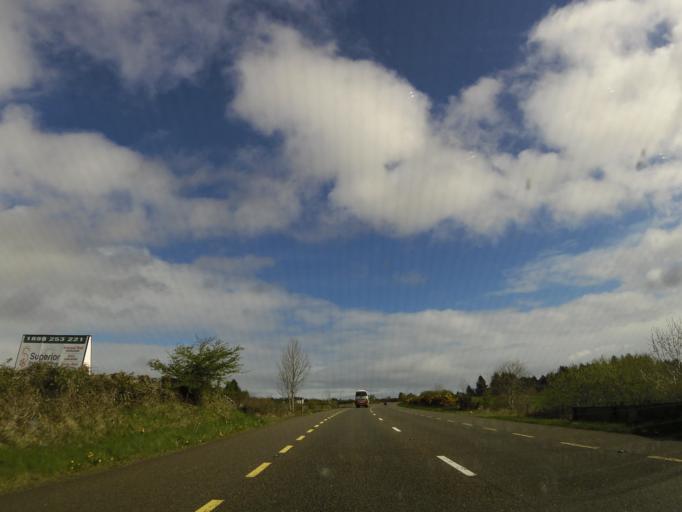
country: IE
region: Connaught
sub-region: Maigh Eo
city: Ballyhaunis
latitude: 53.8991
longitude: -8.7991
